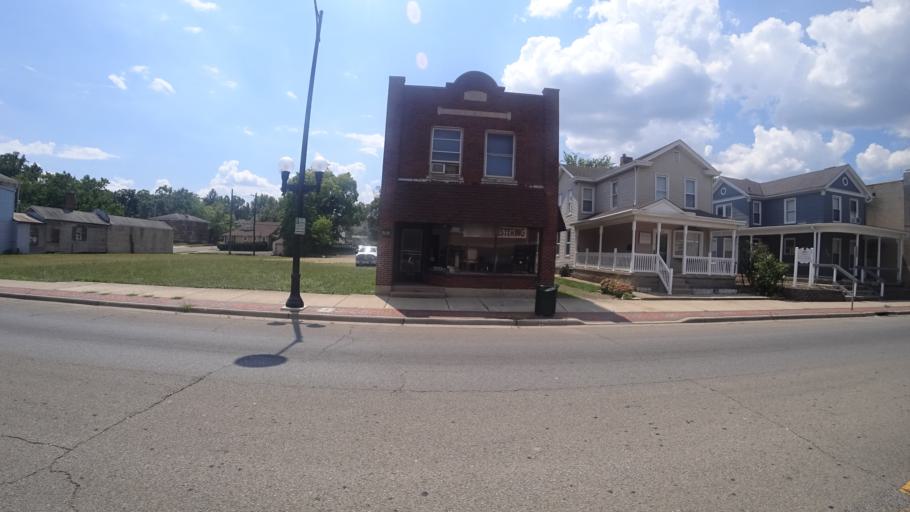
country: US
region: Ohio
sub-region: Butler County
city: Hamilton
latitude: 39.4059
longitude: -84.5721
